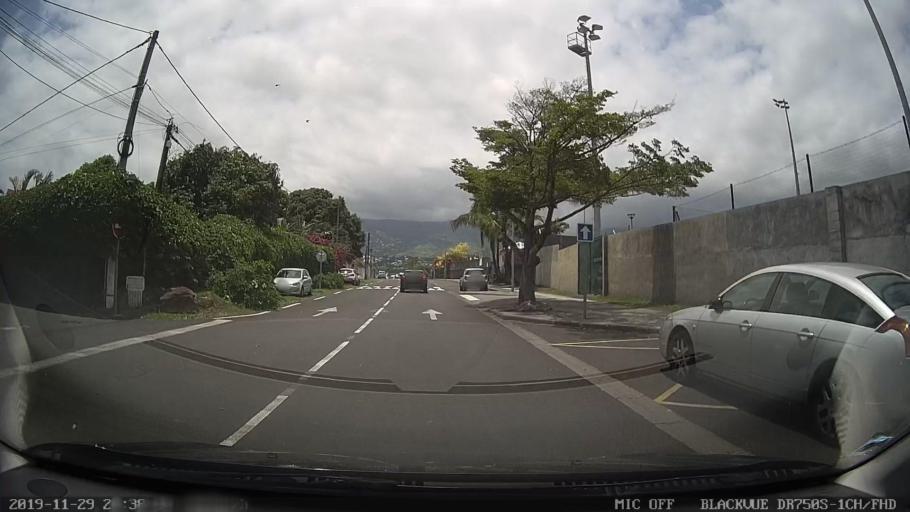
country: RE
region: Reunion
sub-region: Reunion
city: Sainte-Marie
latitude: -20.9034
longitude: 55.5215
